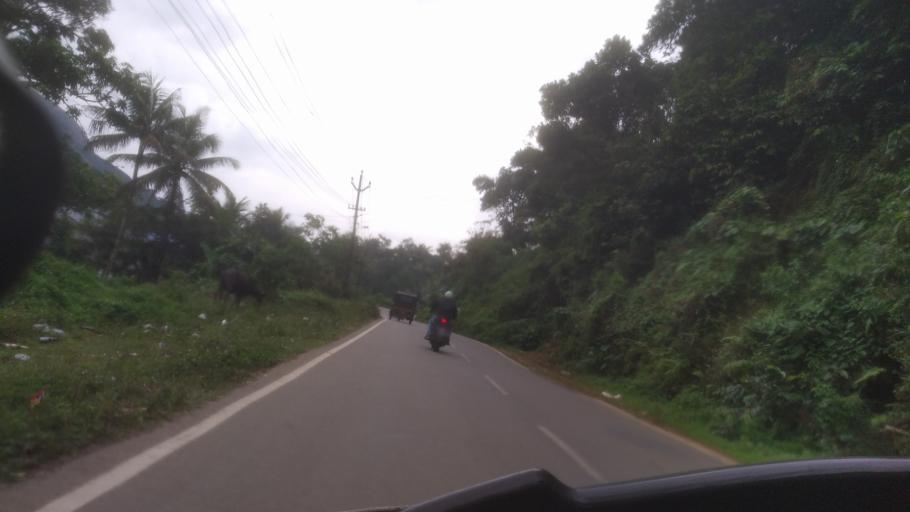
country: IN
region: Kerala
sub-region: Idukki
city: Munnar
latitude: 10.0015
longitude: 76.9677
